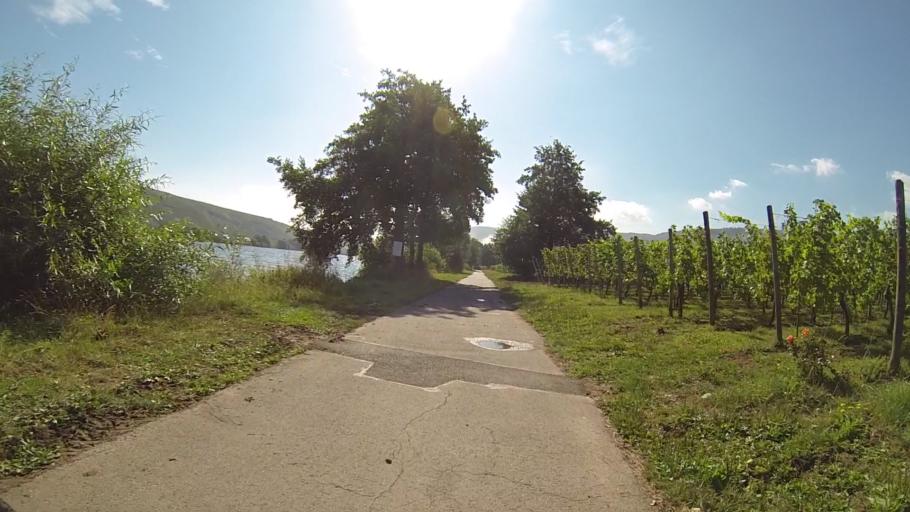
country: DE
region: Rheinland-Pfalz
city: Longuich
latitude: 49.7997
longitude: 6.7895
